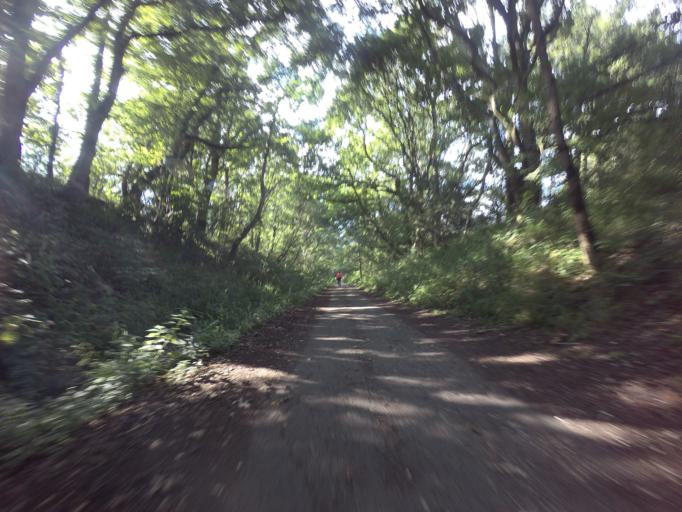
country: GB
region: England
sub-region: East Sussex
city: Horam
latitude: 50.9222
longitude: 0.2542
